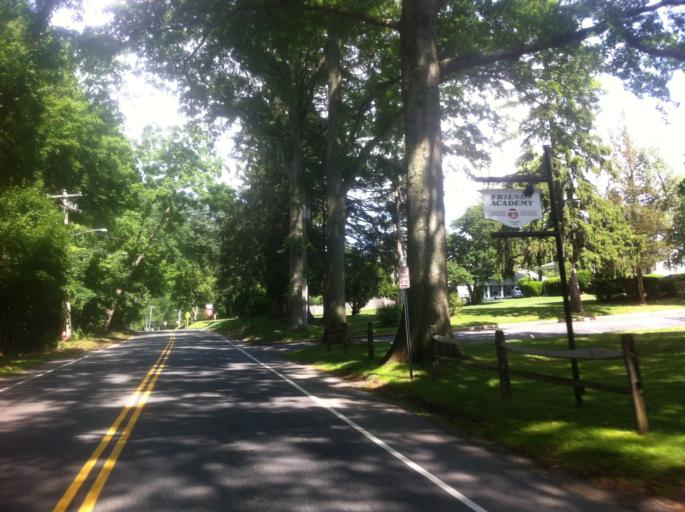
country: US
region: New York
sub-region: Nassau County
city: Locust Valley
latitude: 40.8657
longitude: -73.5999
